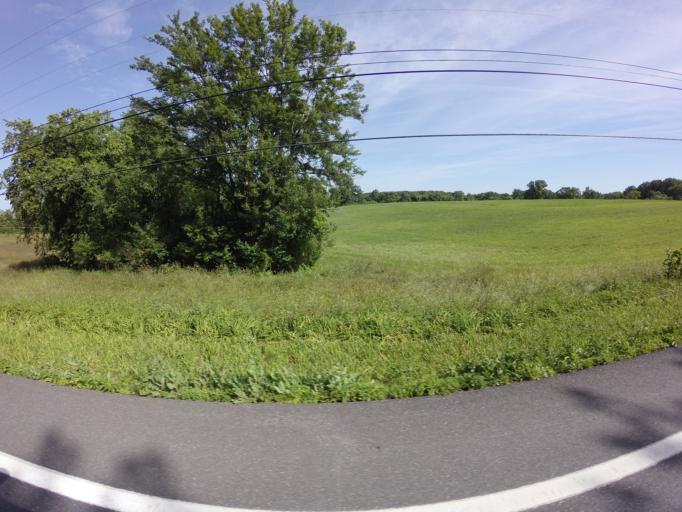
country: US
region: Maryland
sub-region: Frederick County
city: Urbana
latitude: 39.3434
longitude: -77.3186
